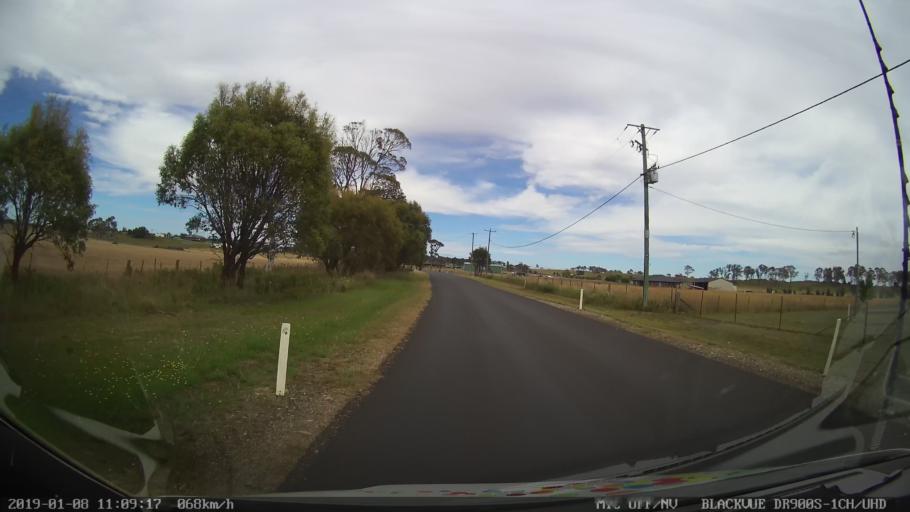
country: AU
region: New South Wales
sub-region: Guyra
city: Guyra
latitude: -30.2250
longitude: 151.6490
